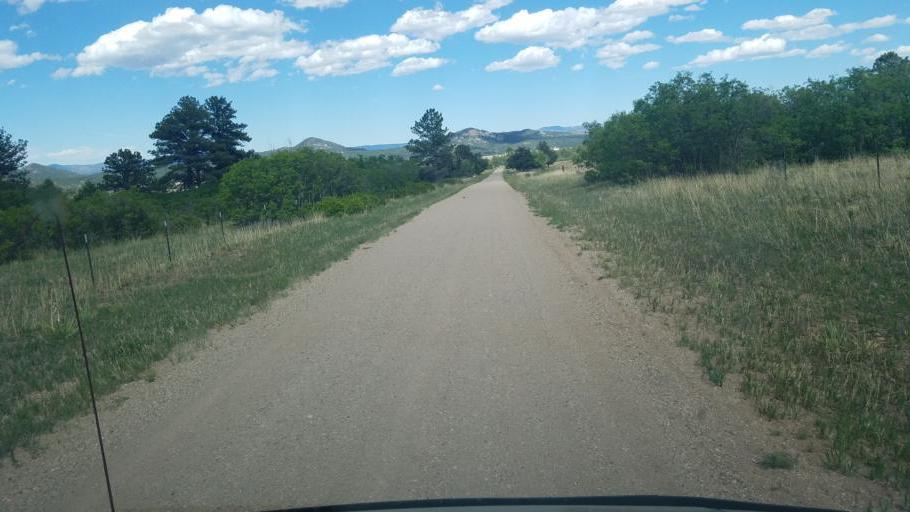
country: US
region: Colorado
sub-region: Custer County
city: Westcliffe
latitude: 38.2253
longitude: -105.6079
